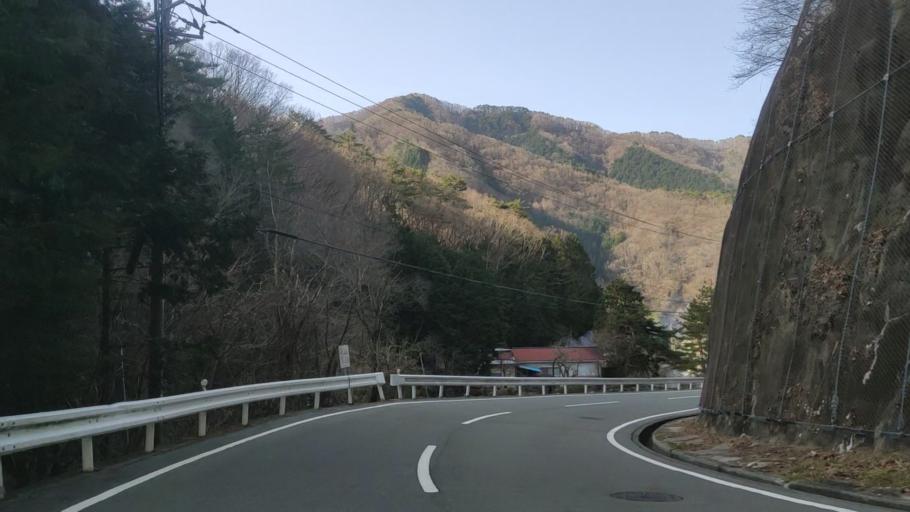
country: JP
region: Yamanashi
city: Fujikawaguchiko
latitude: 35.5524
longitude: 138.6617
